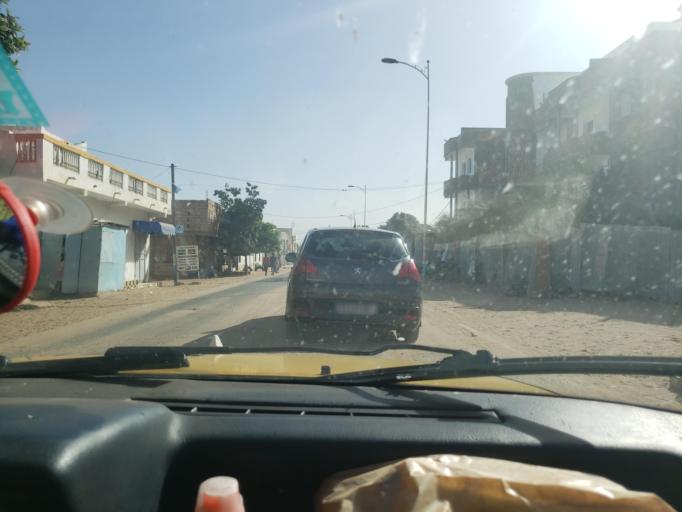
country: SN
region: Louga
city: Louga
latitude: 15.6262
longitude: -16.2136
